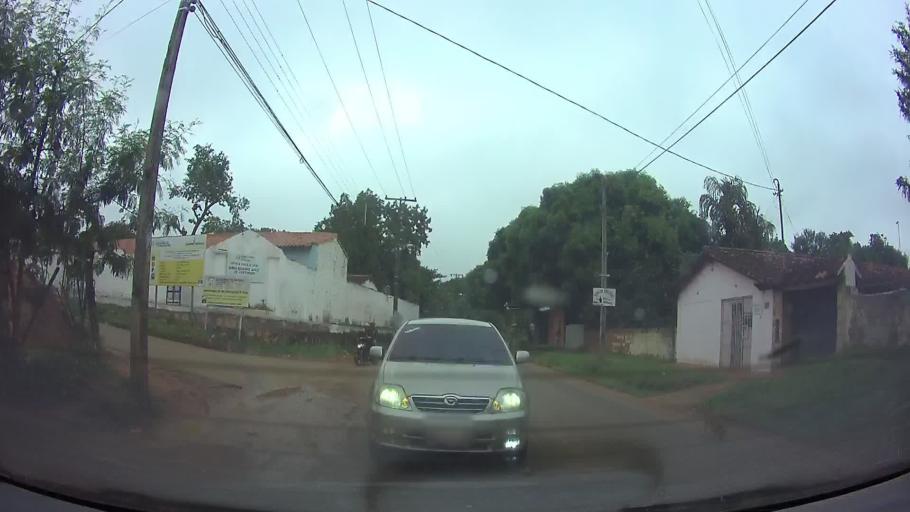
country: PY
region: Central
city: San Lorenzo
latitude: -25.3057
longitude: -57.4909
